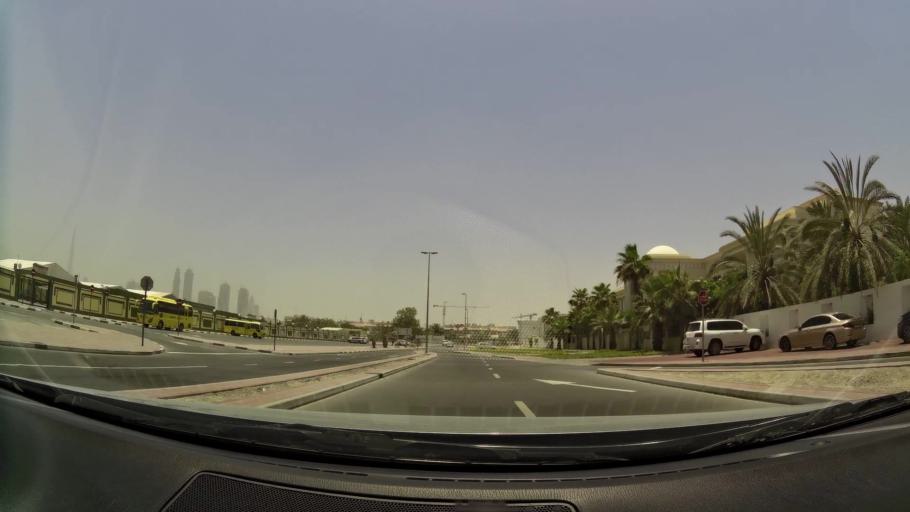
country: AE
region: Dubai
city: Dubai
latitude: 25.1848
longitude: 55.2322
